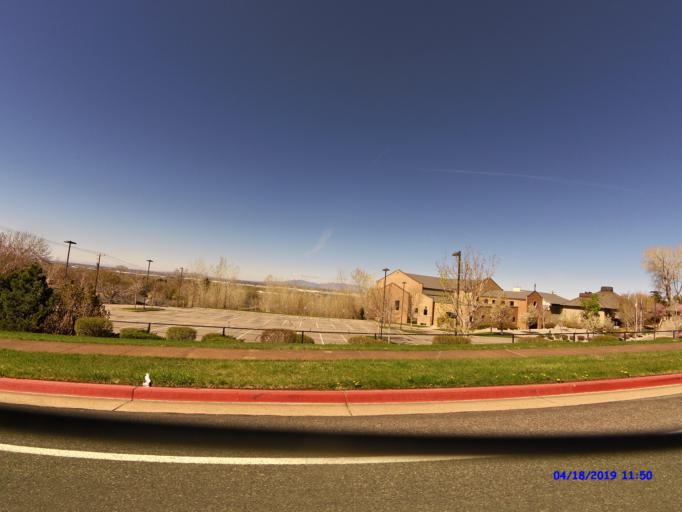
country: US
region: Utah
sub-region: Weber County
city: North Ogden
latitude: 41.2670
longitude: -111.9478
